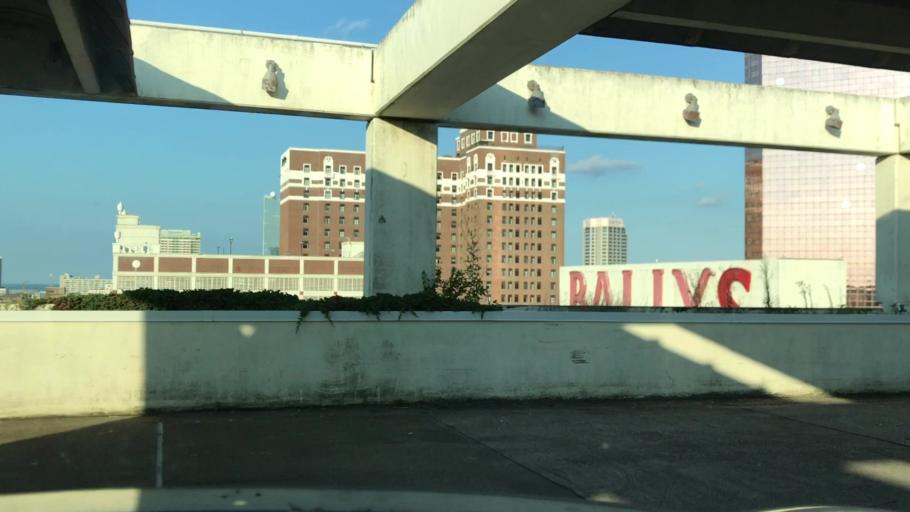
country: US
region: New Jersey
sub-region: Atlantic County
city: Atlantic City
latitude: 39.3574
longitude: -74.4348
